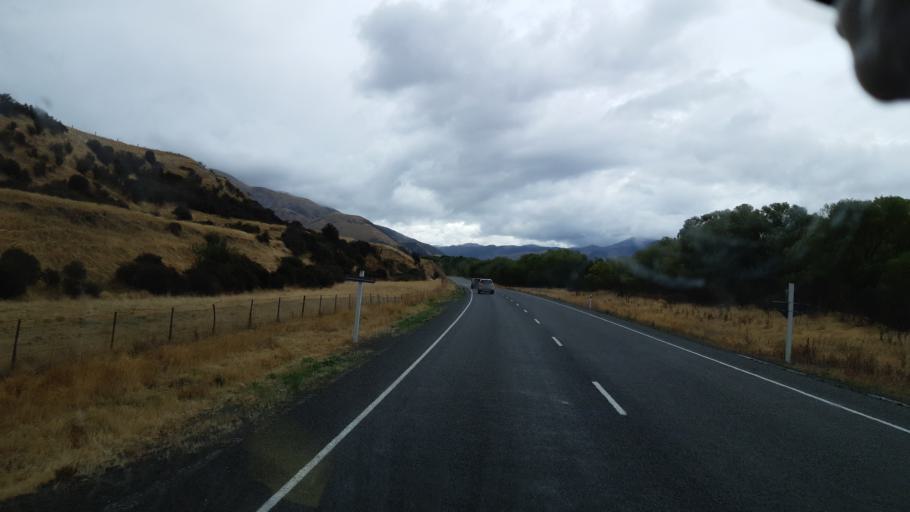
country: NZ
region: Canterbury
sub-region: Hurunui District
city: Amberley
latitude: -42.5787
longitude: 172.7625
